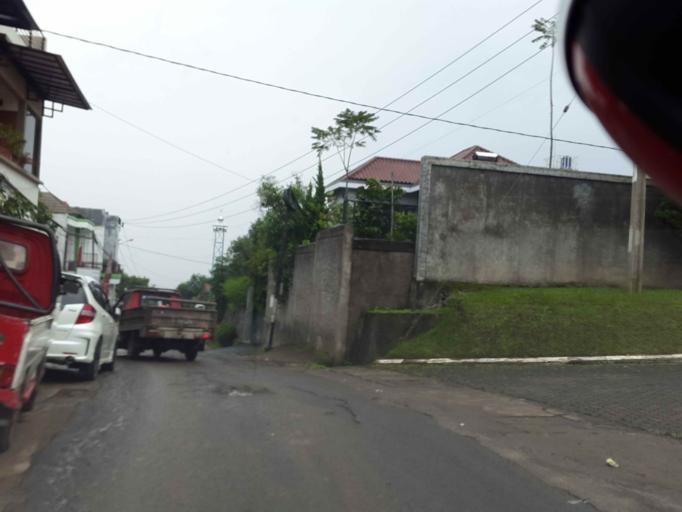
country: ID
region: West Java
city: Cimahi
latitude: -6.8500
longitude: 107.5814
